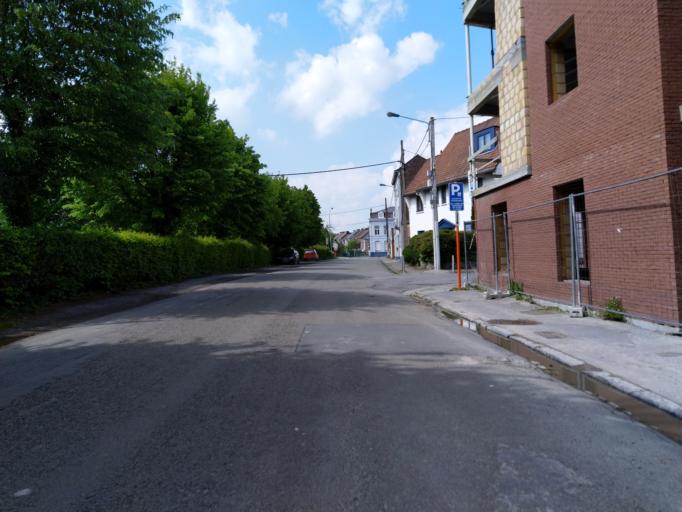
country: BE
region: Wallonia
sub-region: Province du Hainaut
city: Mons
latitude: 50.4484
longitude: 3.9386
